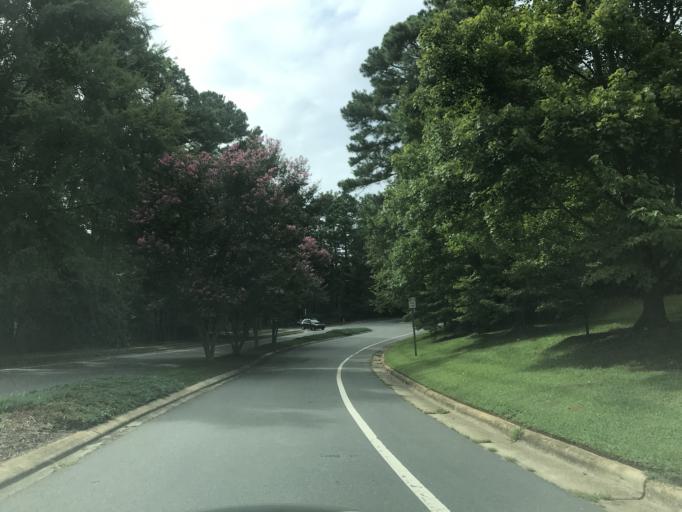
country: US
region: North Carolina
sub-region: Wake County
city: Cary
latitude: 35.7290
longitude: -78.7802
